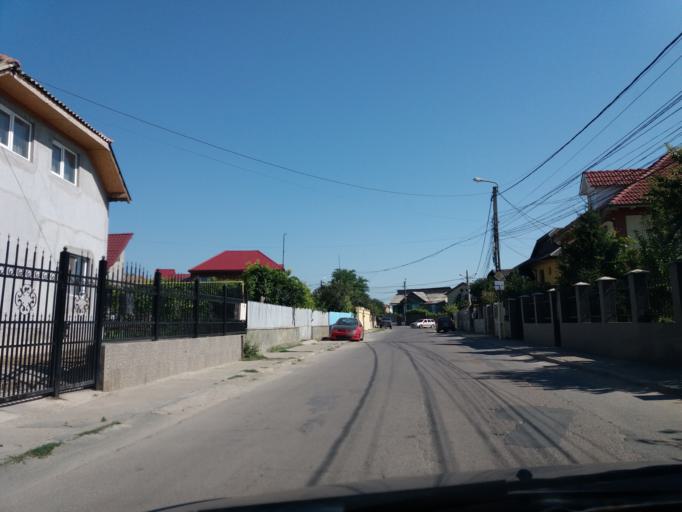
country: RO
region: Constanta
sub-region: Comuna Navodari
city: Navodari
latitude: 44.3292
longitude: 28.6108
